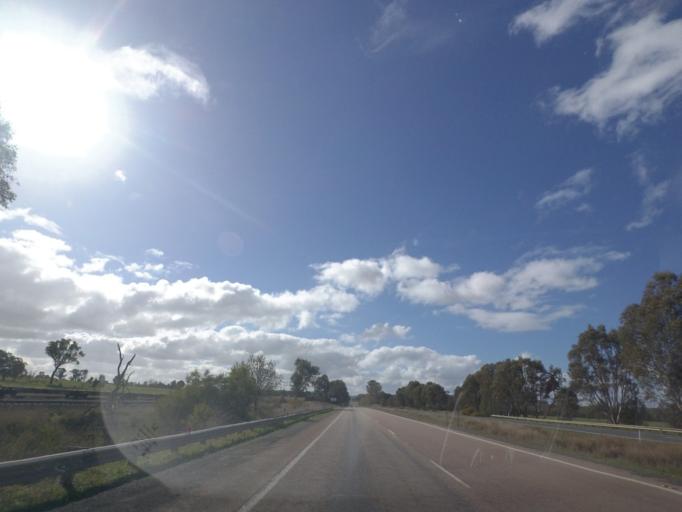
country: AU
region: New South Wales
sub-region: Albury Municipality
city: Lavington
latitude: -35.9822
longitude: 146.9993
